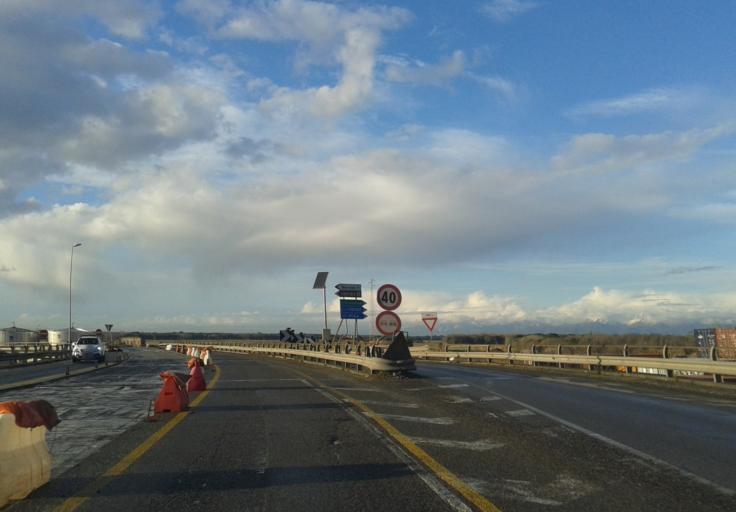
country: IT
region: Tuscany
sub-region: Provincia di Livorno
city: Livorno
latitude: 43.5869
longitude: 10.3238
